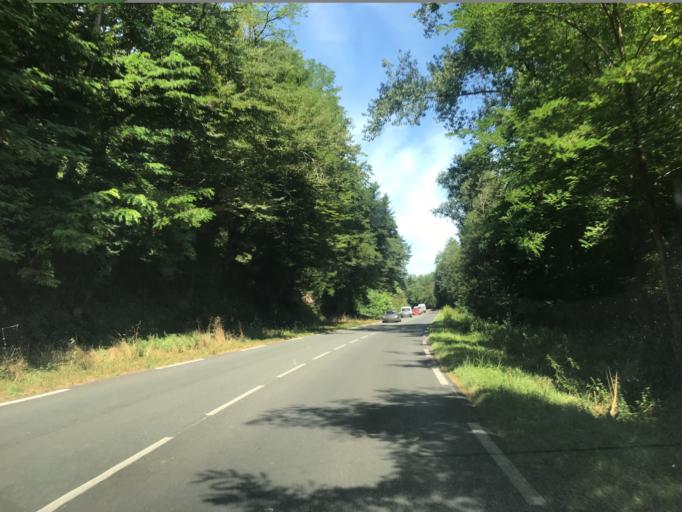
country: FR
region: Aquitaine
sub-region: Departement de la Dordogne
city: Domme
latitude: 44.8314
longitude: 1.2191
